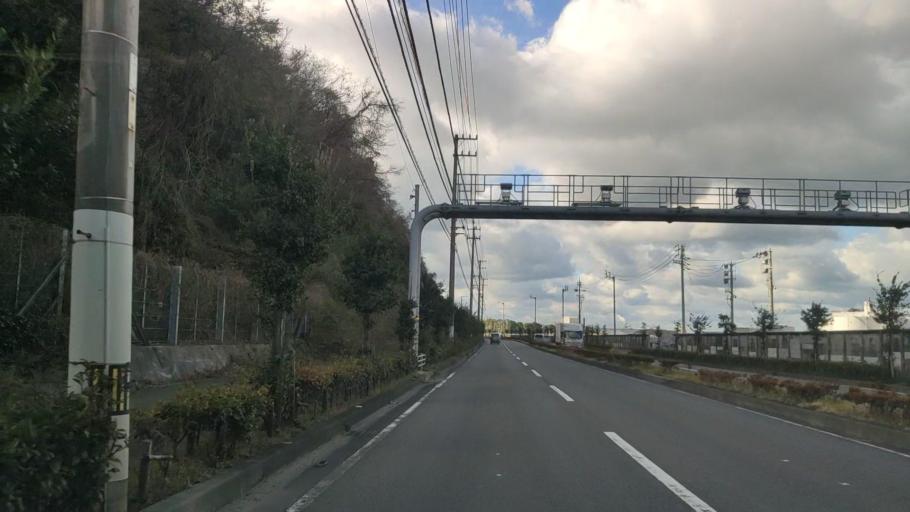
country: JP
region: Ehime
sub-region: Shikoku-chuo Shi
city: Matsuyama
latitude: 33.8462
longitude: 132.7108
